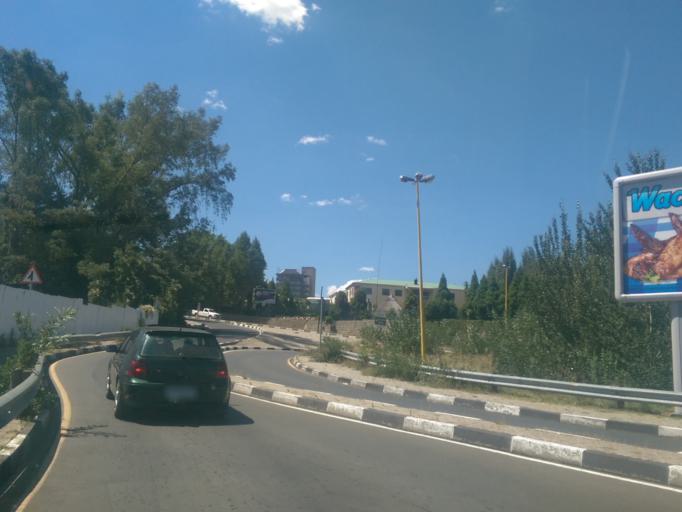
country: LS
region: Maseru
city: Maseru
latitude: -29.3156
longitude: 27.4779
